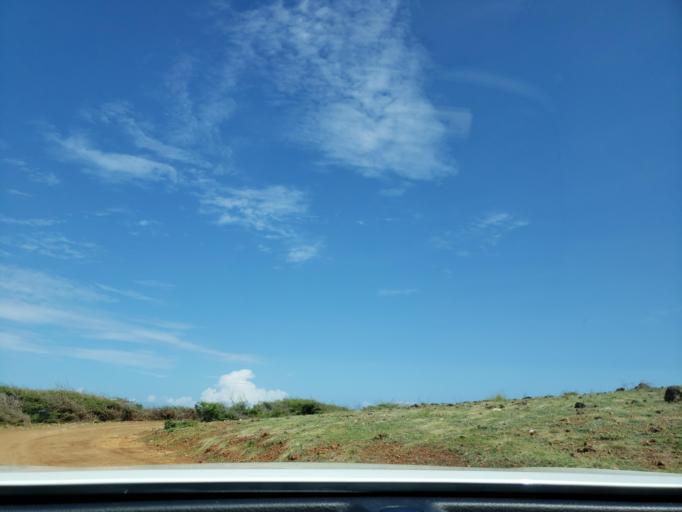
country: CW
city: Barber
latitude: 12.3638
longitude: -69.1125
